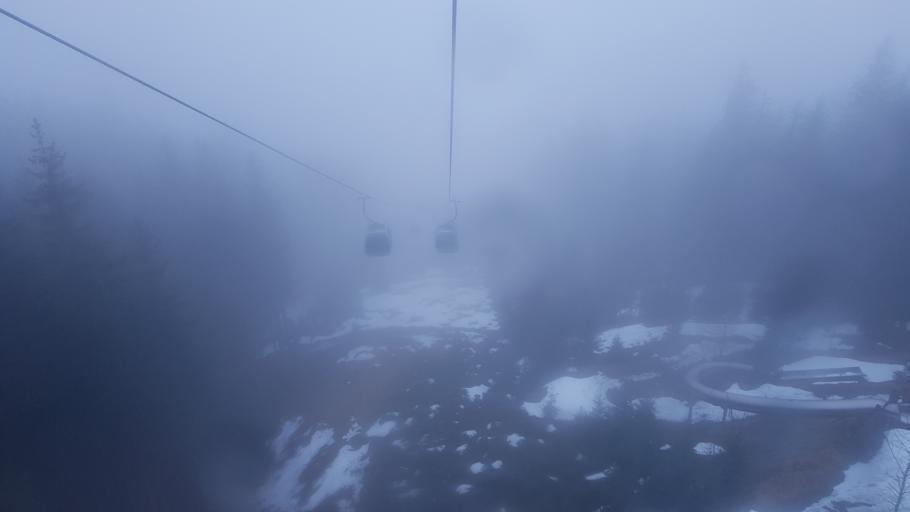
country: AT
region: Salzburg
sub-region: Politischer Bezirk Zell am See
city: Neukirchen am Grossvenediger
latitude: 47.2653
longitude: 12.2806
